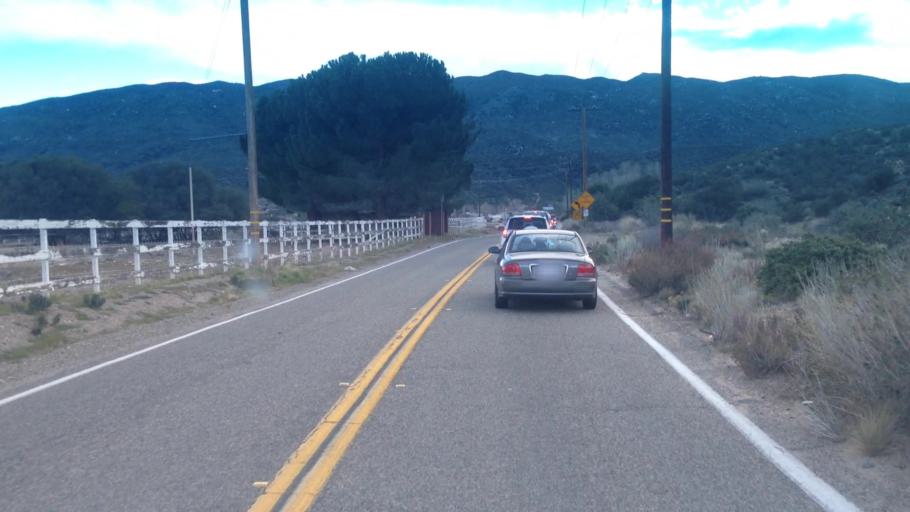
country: US
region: California
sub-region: San Bernardino County
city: Oak Hills
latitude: 34.3306
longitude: -117.3975
